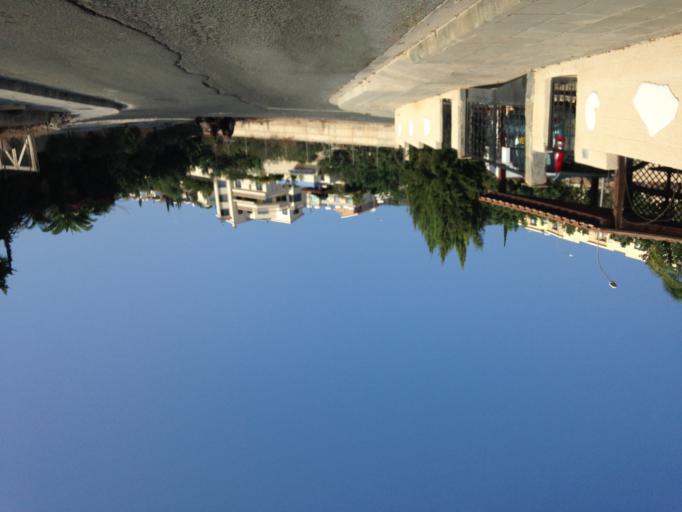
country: CY
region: Pafos
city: Pegeia
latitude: 34.8826
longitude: 32.3862
